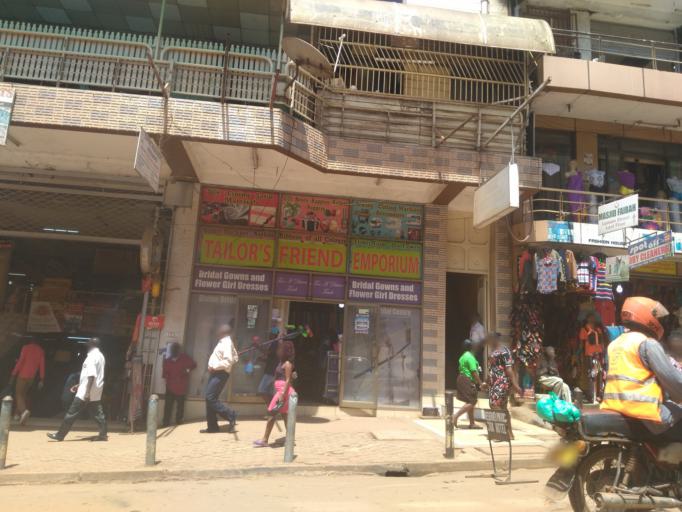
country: UG
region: Central Region
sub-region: Kampala District
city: Kampala
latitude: 0.3128
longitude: 32.5782
